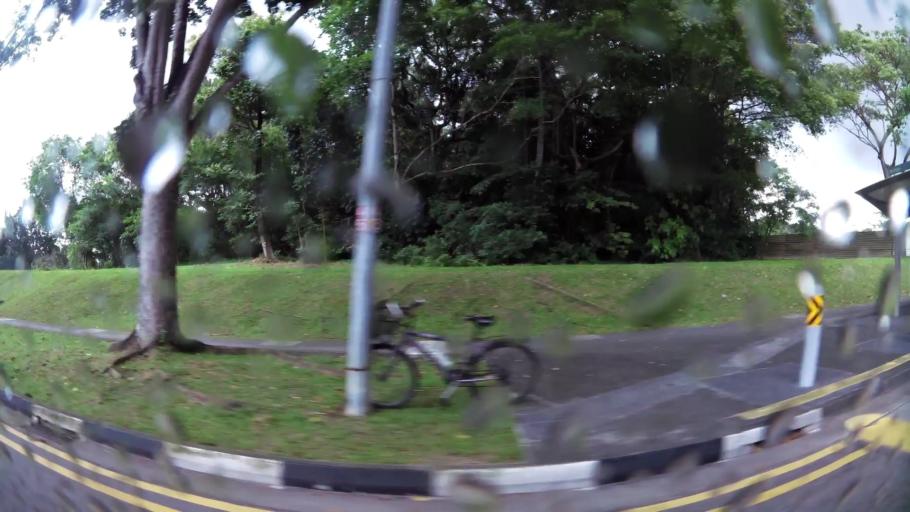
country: MY
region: Johor
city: Kampung Pasir Gudang Baru
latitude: 1.3999
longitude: 103.8724
